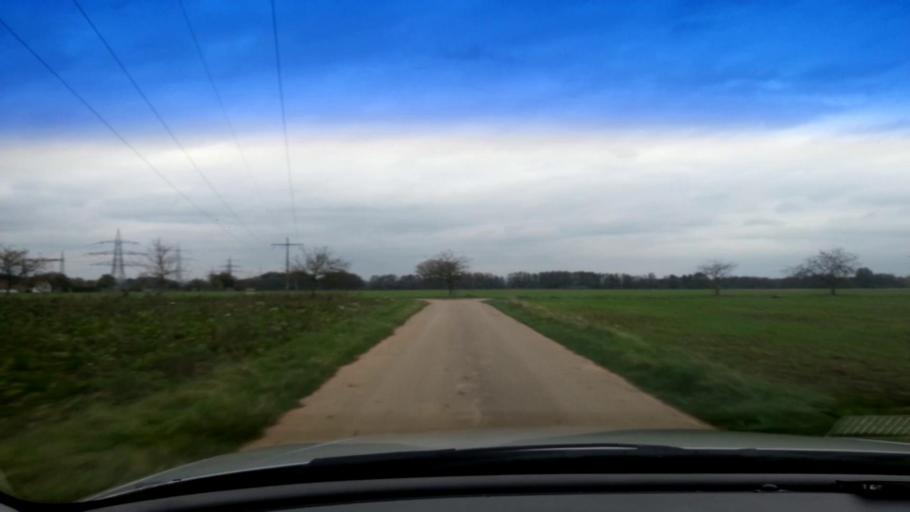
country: DE
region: Bavaria
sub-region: Upper Franconia
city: Bischberg
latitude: 49.9266
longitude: 10.8308
